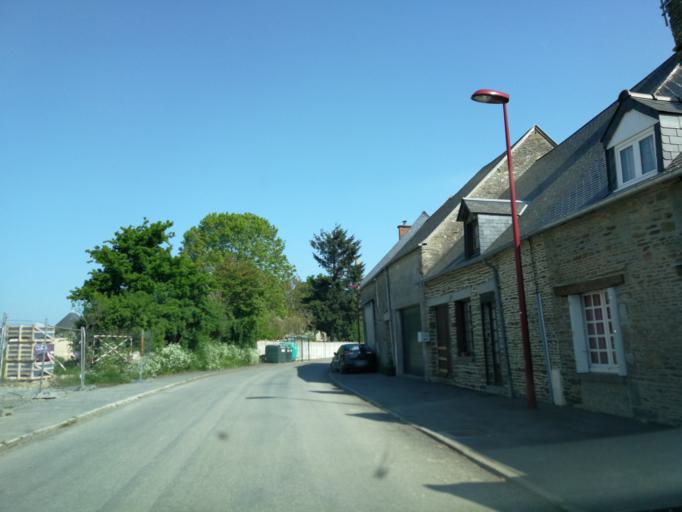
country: FR
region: Lower Normandy
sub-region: Departement de la Manche
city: Pontorson
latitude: 48.6011
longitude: -1.4742
